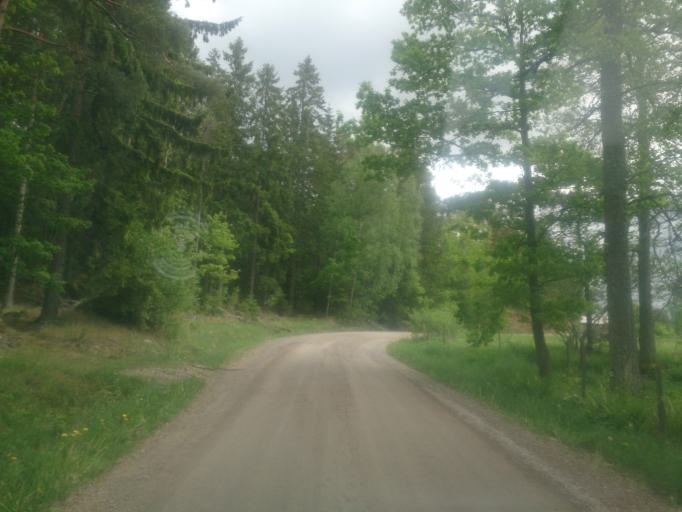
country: SE
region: OEstergoetland
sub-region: Atvidabergs Kommun
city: Atvidaberg
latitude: 58.2278
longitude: 16.0731
